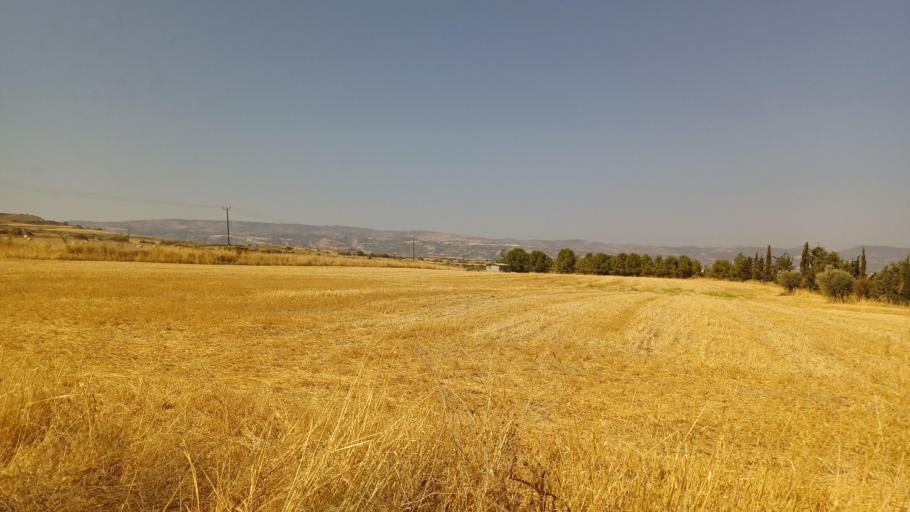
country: CY
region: Pafos
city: Polis
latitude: 35.0444
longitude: 32.4584
